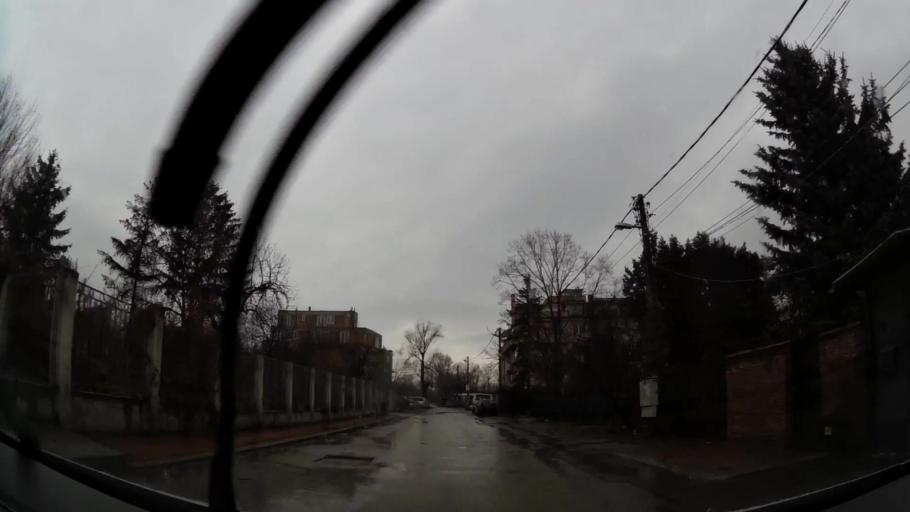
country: BG
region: Sofia-Capital
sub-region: Stolichna Obshtina
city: Sofia
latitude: 42.6496
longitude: 23.3297
